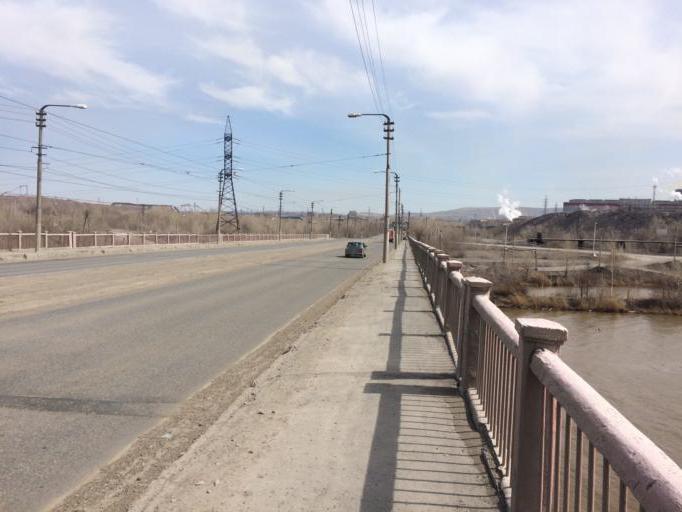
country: RU
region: Chelyabinsk
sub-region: Gorod Magnitogorsk
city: Magnitogorsk
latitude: 53.4509
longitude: 59.0171
